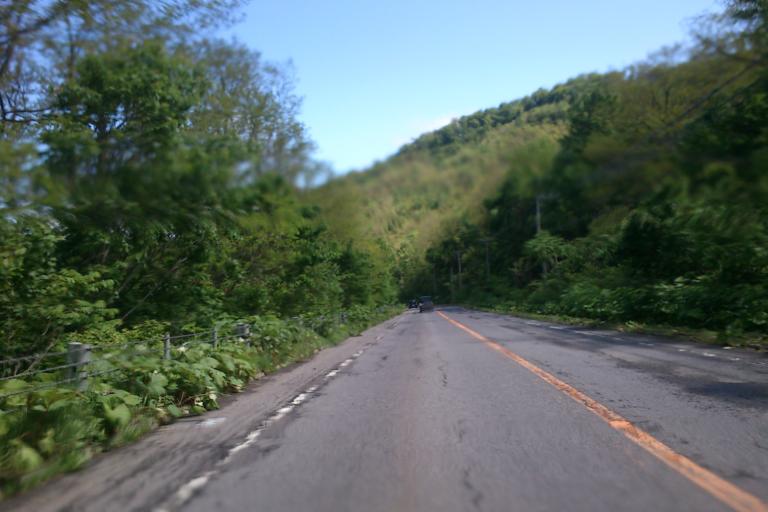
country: JP
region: Hokkaido
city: Ishikari
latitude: 43.5458
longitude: 141.3970
